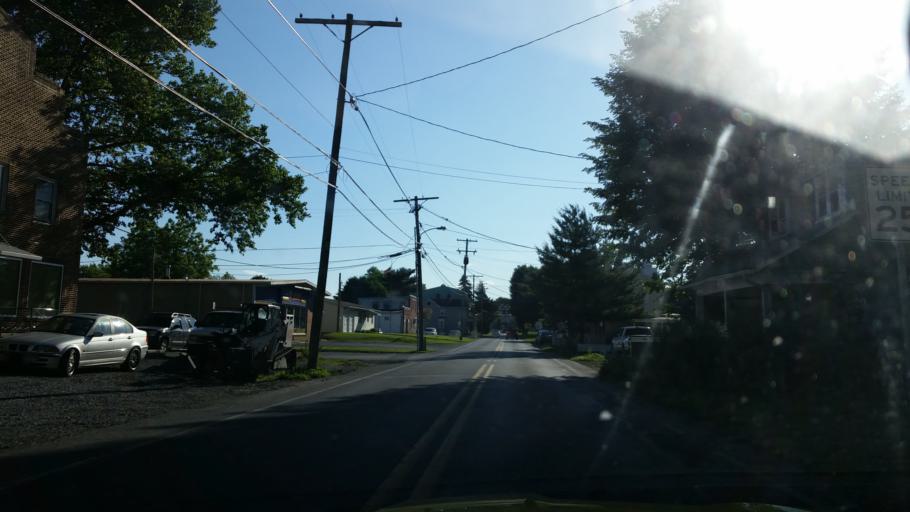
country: US
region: Pennsylvania
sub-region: Lebanon County
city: Avon
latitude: 40.3460
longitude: -76.3874
